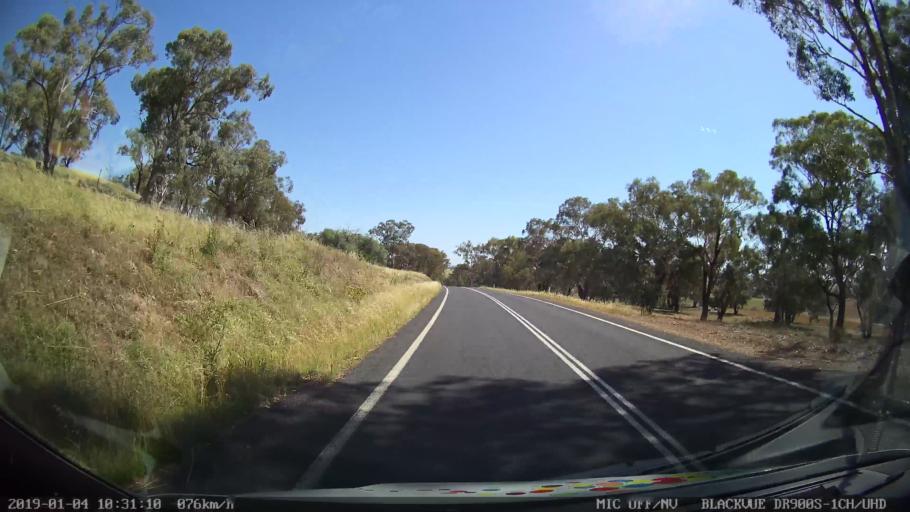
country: AU
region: New South Wales
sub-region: Cabonne
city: Canowindra
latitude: -33.3377
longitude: 148.6316
